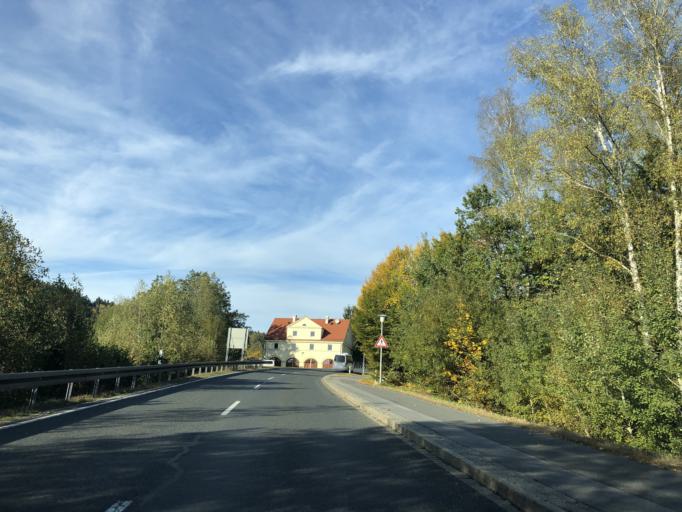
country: DE
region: Bavaria
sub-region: Lower Bavaria
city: Teisnach
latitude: 49.0426
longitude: 12.9951
